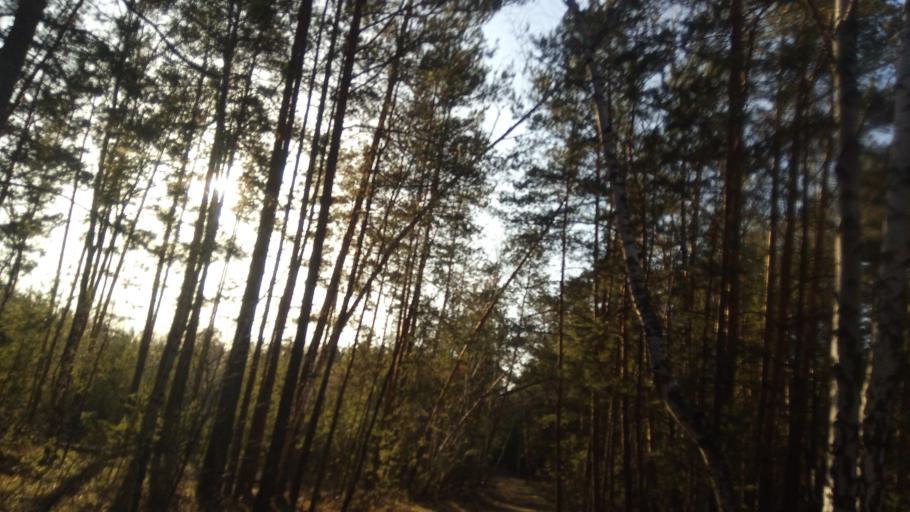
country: RU
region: Chelyabinsk
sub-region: Gorod Chelyabinsk
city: Chelyabinsk
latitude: 55.1593
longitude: 61.3355
